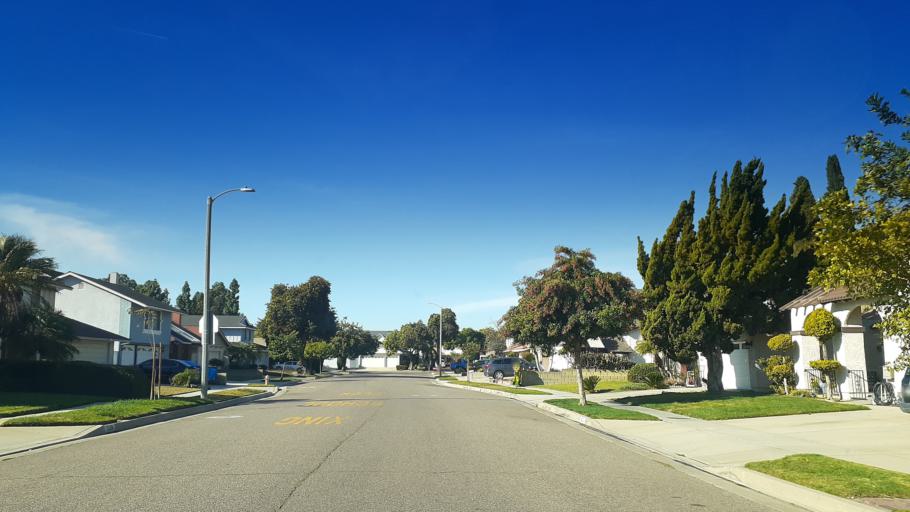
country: US
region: California
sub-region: Los Angeles County
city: Cerritos
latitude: 33.8619
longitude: -118.0684
